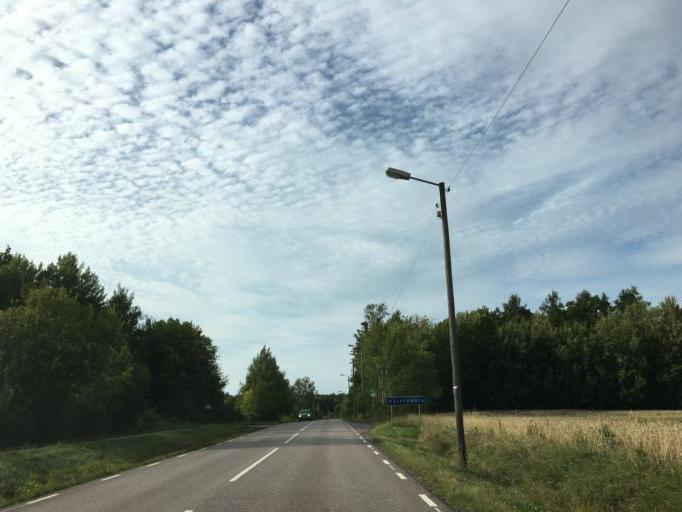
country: SE
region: Soedermanland
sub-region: Eskilstuna Kommun
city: Torshalla
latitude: 59.4409
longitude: 16.4560
